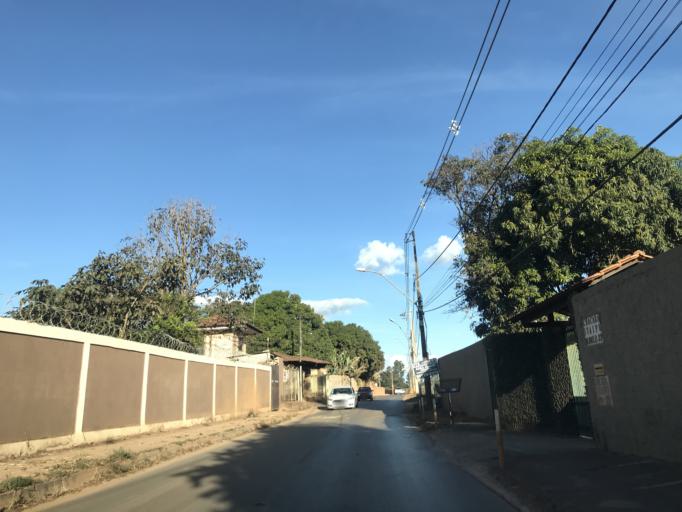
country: BR
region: Federal District
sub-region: Brasilia
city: Brasilia
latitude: -15.8814
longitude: -47.7758
